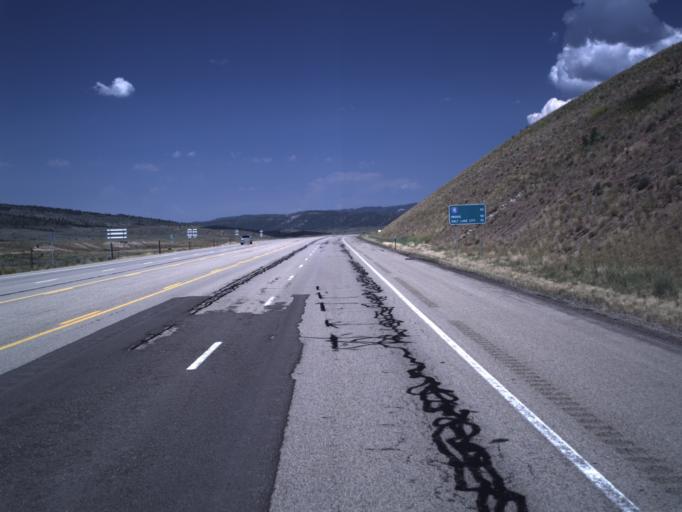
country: US
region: Utah
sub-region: Carbon County
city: Helper
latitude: 39.8631
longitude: -111.0275
